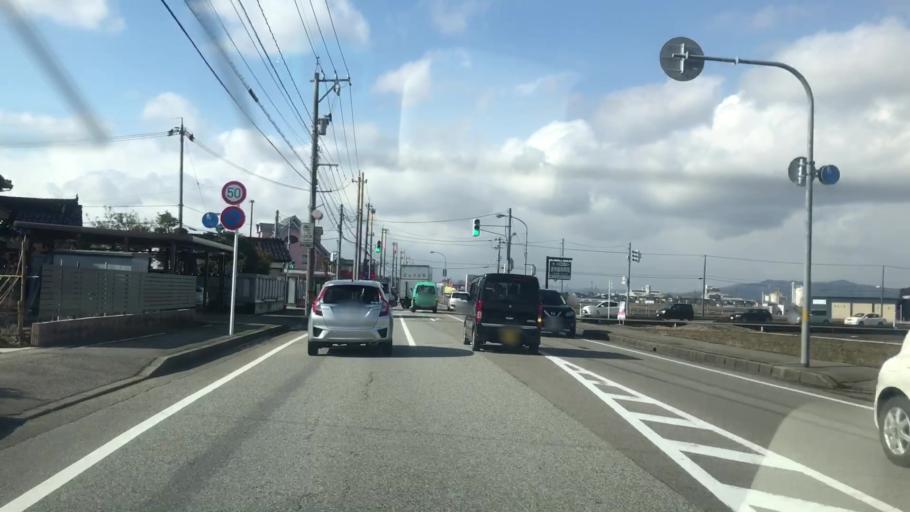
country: JP
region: Toyama
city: Nishishinminato
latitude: 36.7235
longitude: 137.0689
